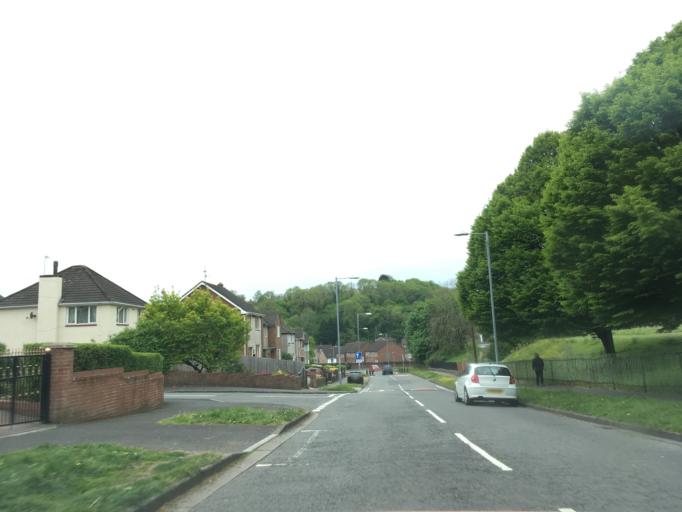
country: GB
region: Wales
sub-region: Newport
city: Caerleon
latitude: 51.5916
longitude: -2.9389
